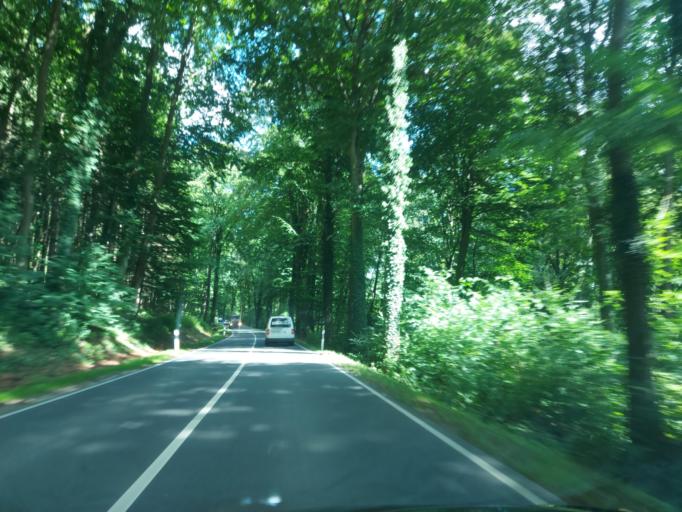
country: DE
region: Lower Saxony
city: Hagen
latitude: 52.1801
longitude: 8.0106
